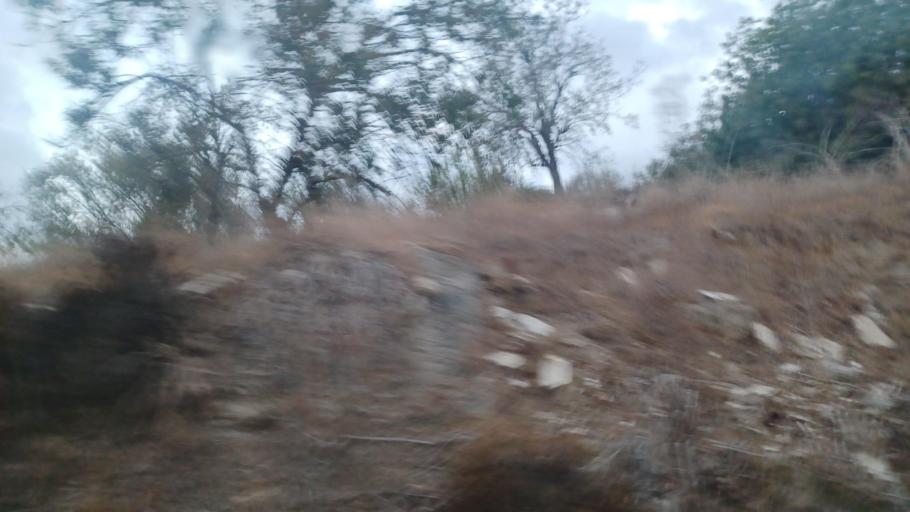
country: CY
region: Pafos
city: Mesogi
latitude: 34.8498
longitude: 32.5297
